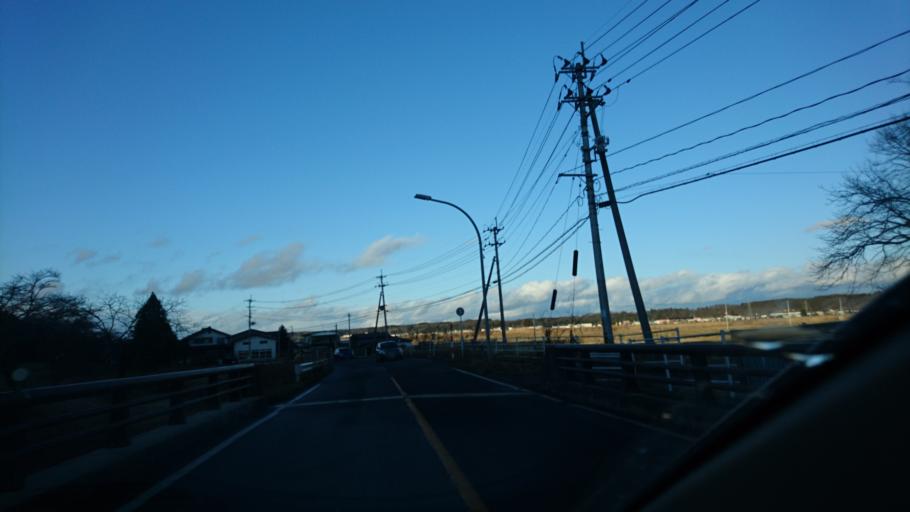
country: JP
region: Miyagi
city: Furukawa
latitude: 38.6358
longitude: 140.8718
